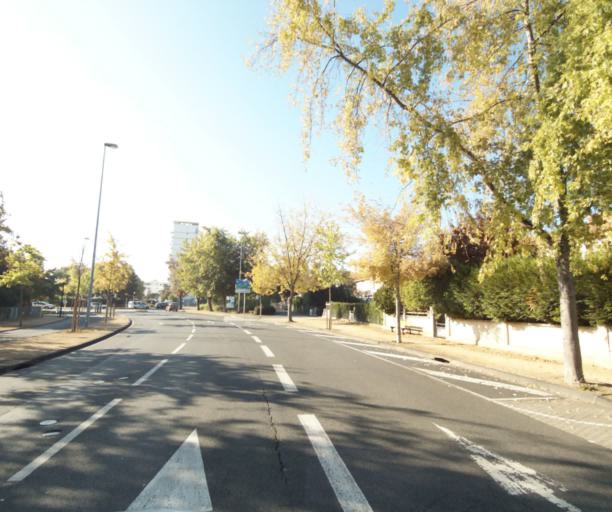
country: FR
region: Auvergne
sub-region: Departement du Puy-de-Dome
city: Gerzat
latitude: 45.8049
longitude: 3.1187
